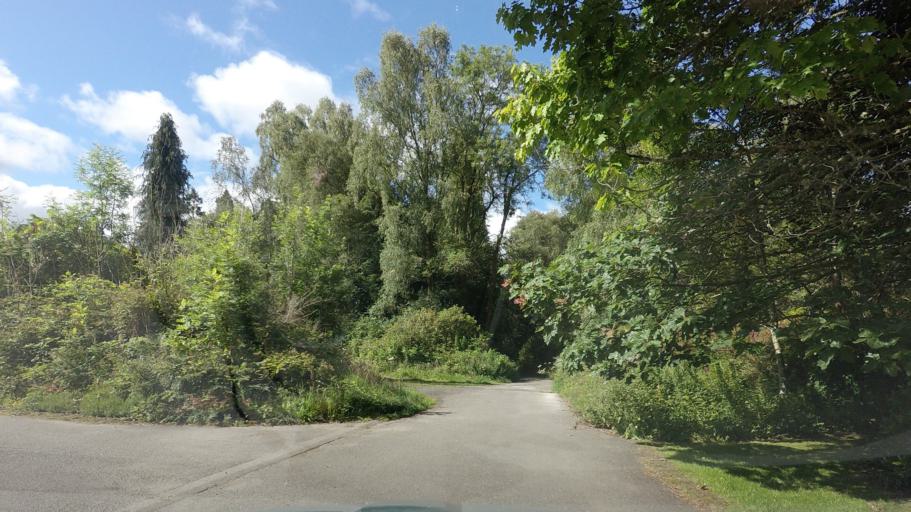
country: GB
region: Scotland
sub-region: Stirling
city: Killearn
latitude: 56.0680
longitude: -4.4804
